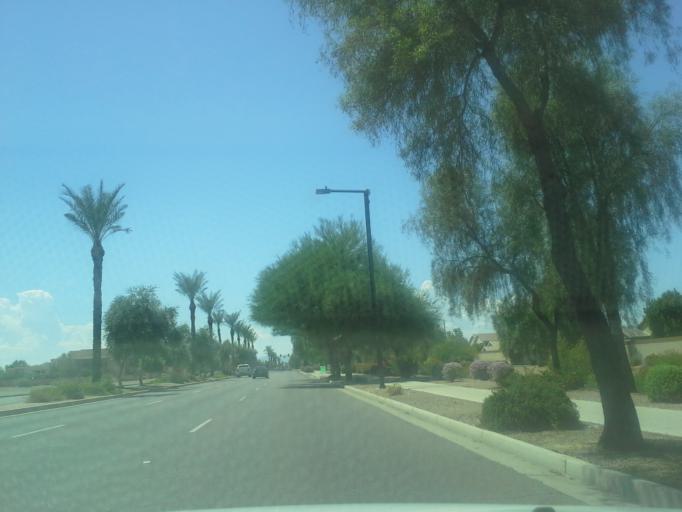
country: US
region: Arizona
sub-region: Maricopa County
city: Glendale
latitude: 33.5383
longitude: -112.2085
